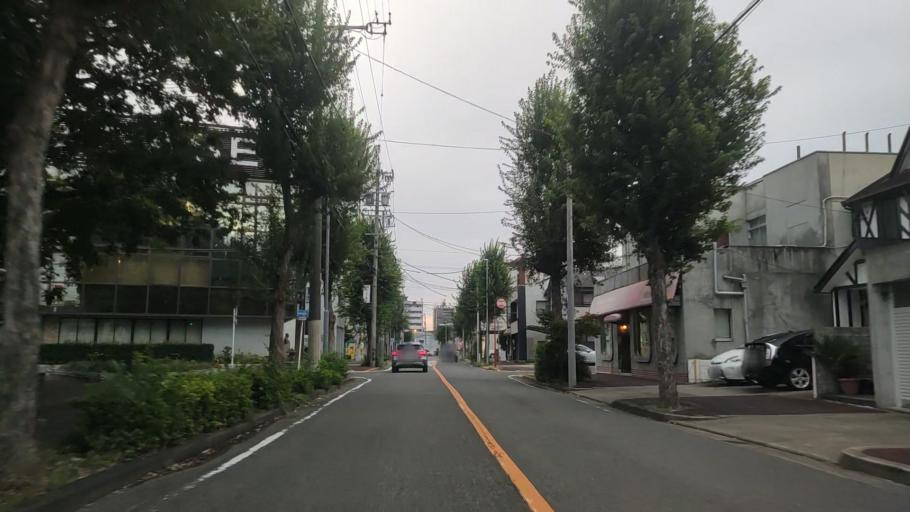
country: JP
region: Aichi
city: Nagoya-shi
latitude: 35.1912
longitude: 136.8955
